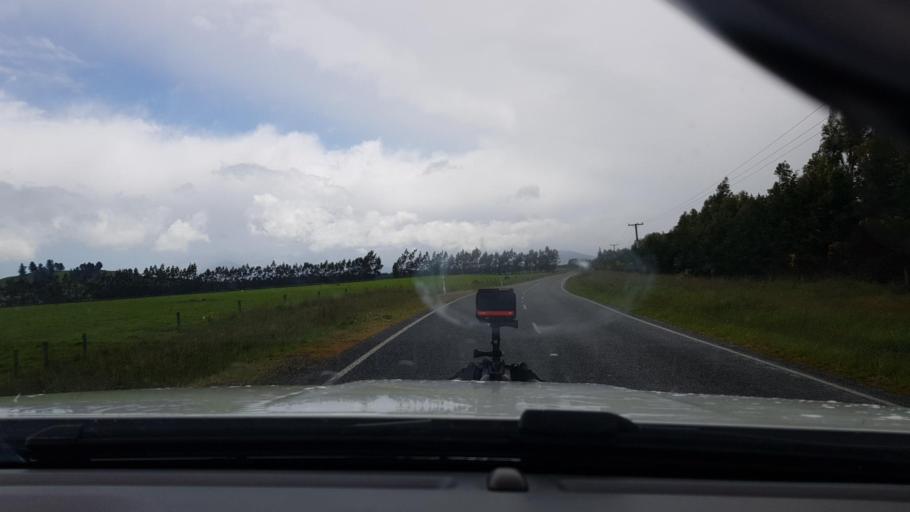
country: NZ
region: Southland
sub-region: Southland District
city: Winton
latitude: -45.7412
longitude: 168.3965
